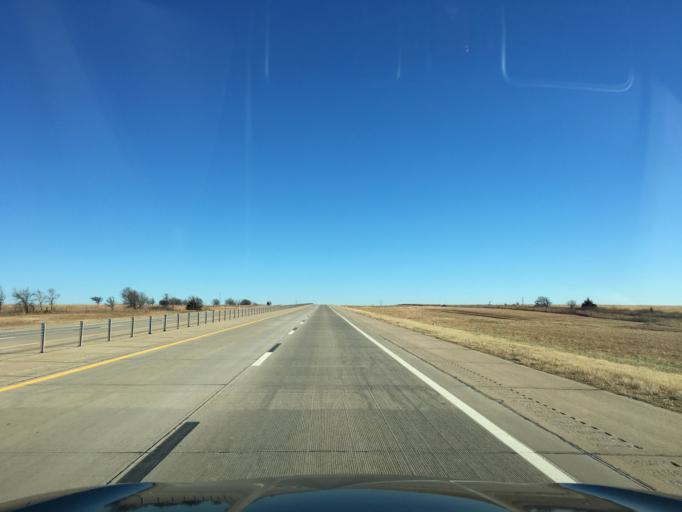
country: US
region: Oklahoma
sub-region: Noble County
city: Perry
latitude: 36.3921
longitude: -97.1256
